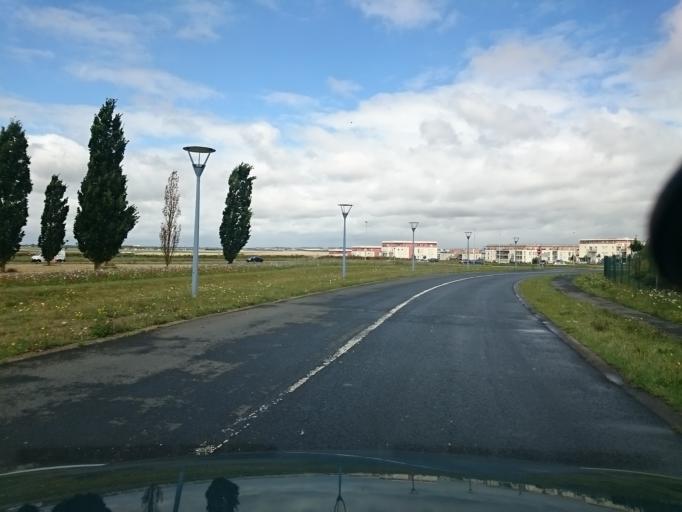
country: FR
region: Lower Normandy
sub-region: Departement du Calvados
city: Fleury-sur-Orne
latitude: 49.1377
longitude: -0.3748
